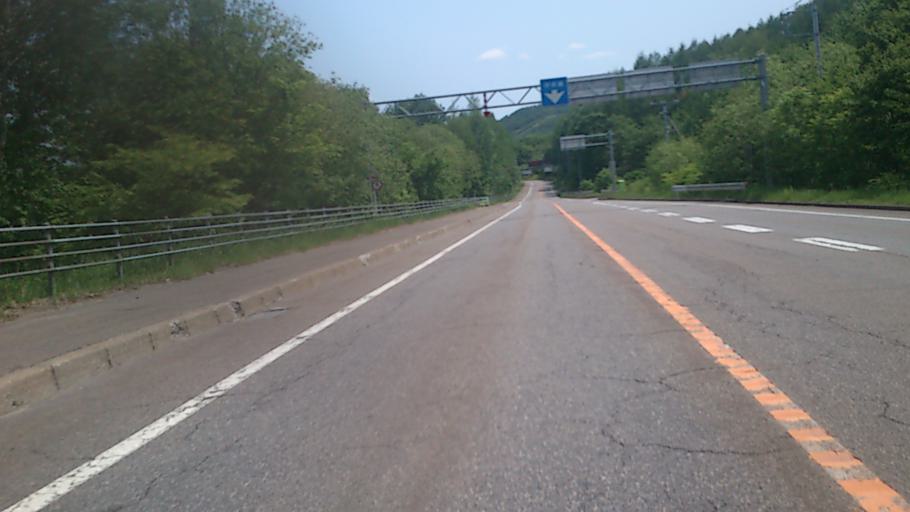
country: JP
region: Hokkaido
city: Otofuke
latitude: 43.2372
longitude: 143.5385
